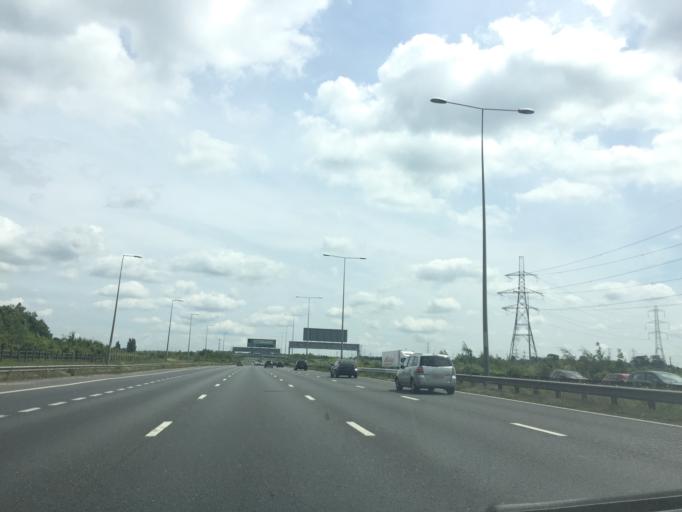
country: GB
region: England
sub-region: Kent
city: Swanscombe
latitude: 51.4250
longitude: 0.3341
